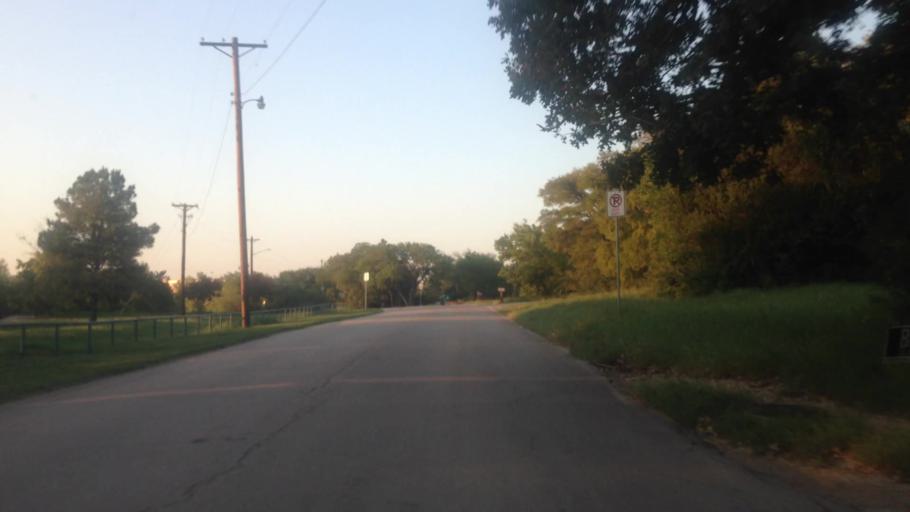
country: US
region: Texas
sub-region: Denton County
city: Denton
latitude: 33.2015
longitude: -97.1545
